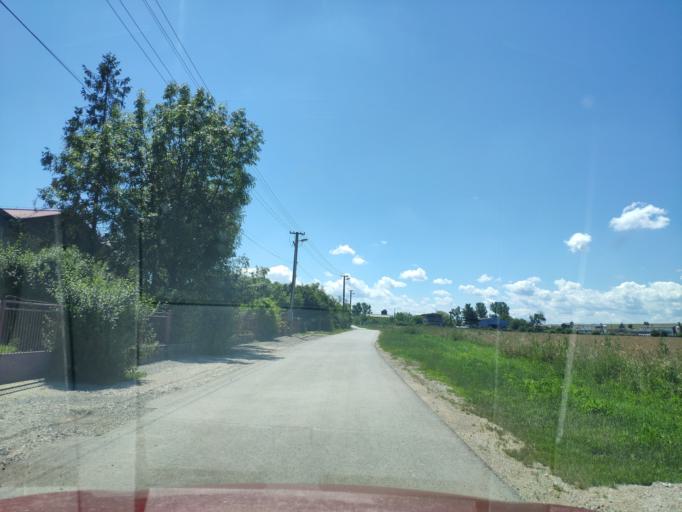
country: HU
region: Borsod-Abauj-Zemplen
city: Ozd
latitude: 48.3368
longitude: 20.2966
